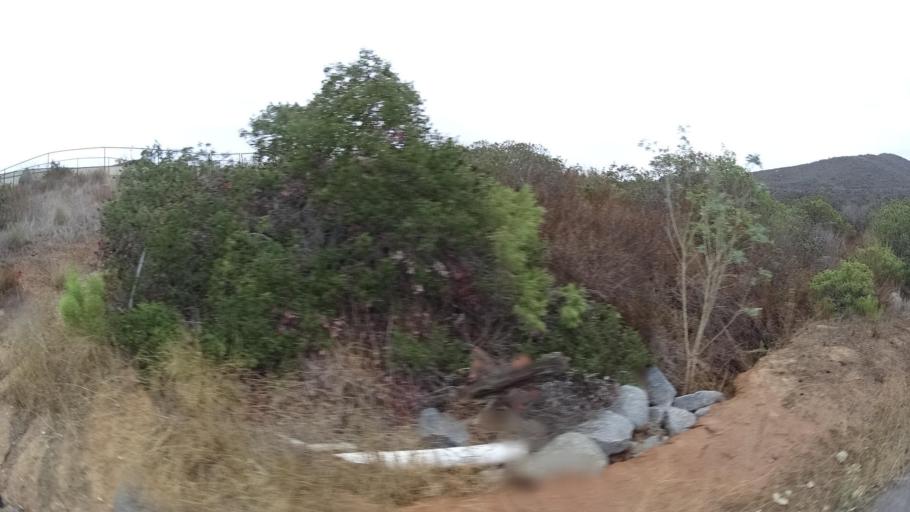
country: US
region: California
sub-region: San Diego County
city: Escondido
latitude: 33.0875
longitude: -117.1141
